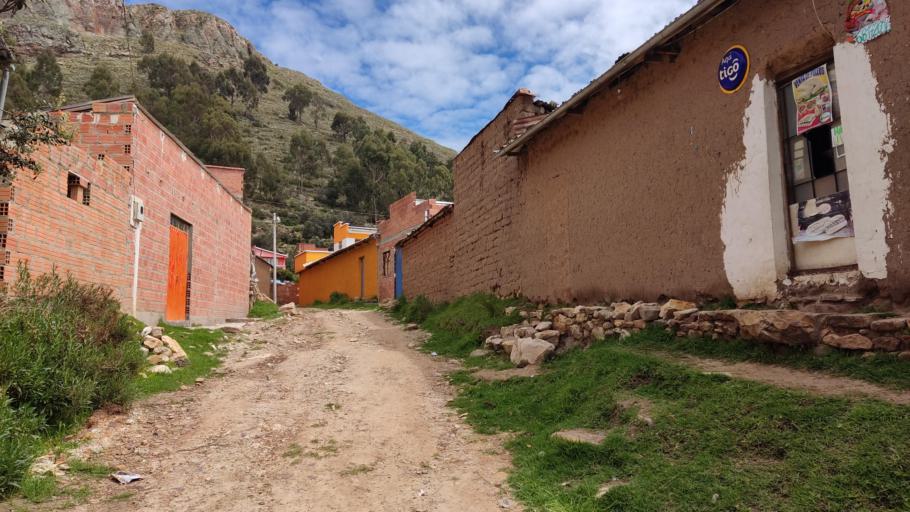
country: BO
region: La Paz
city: Batallas
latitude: -16.3463
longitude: -68.6392
